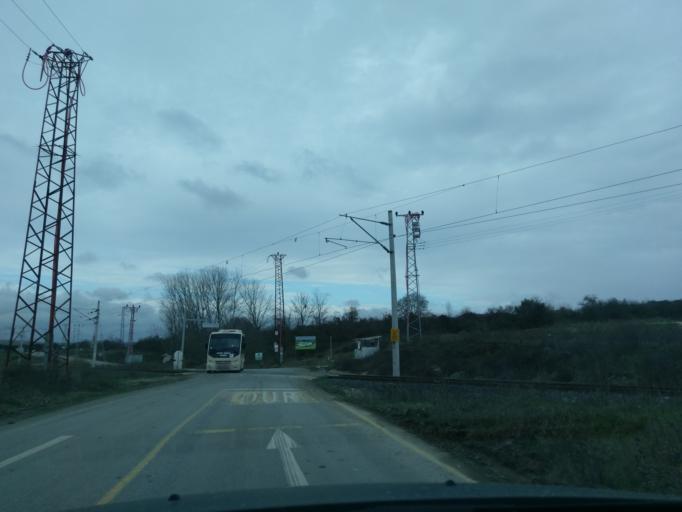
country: TR
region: Istanbul
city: Catalca
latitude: 41.2047
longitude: 28.3854
